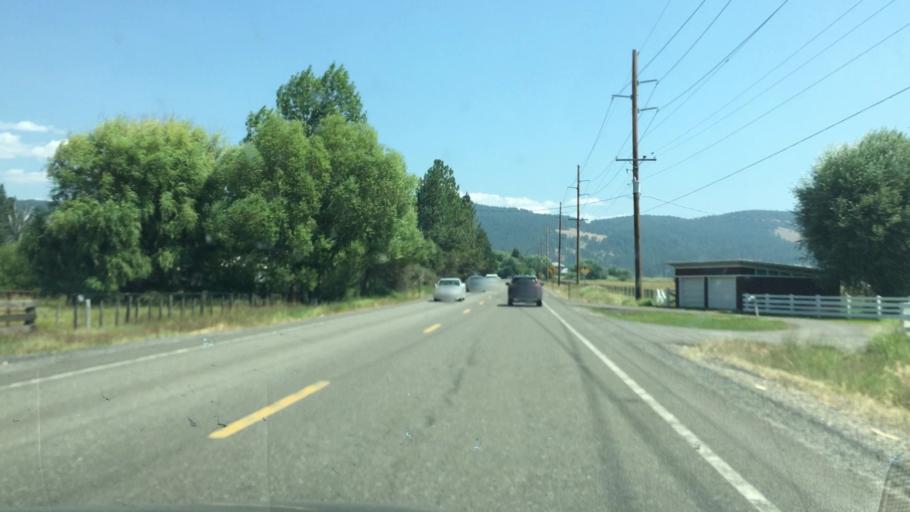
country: US
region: Idaho
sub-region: Valley County
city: McCall
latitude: 44.9631
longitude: -116.2557
